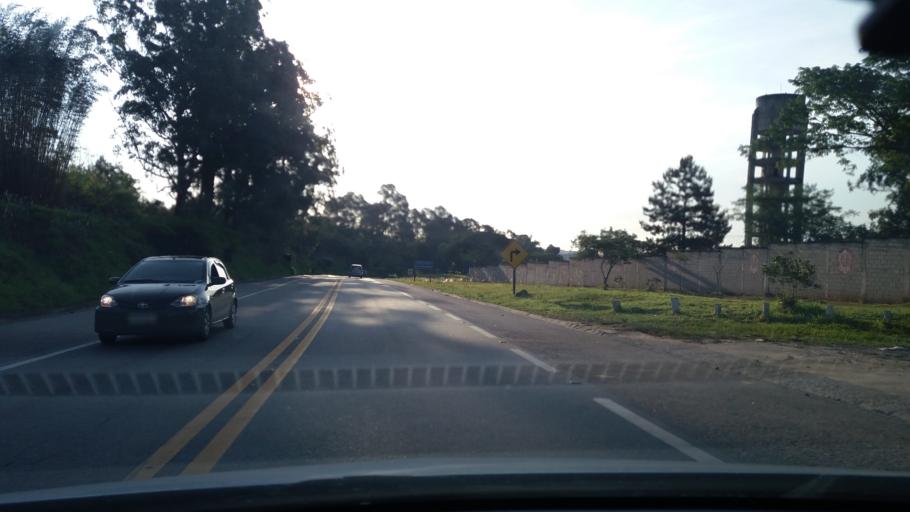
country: BR
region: Sao Paulo
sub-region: Franco Da Rocha
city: Franco da Rocha
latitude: -23.3323
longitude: -46.6826
